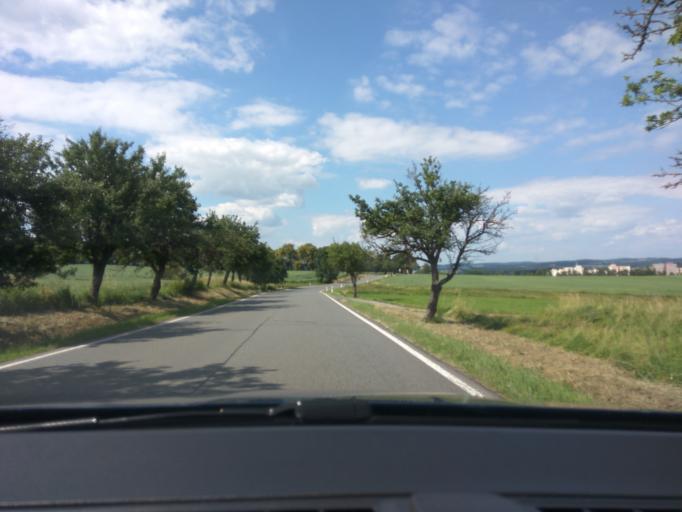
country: CZ
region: Jihocesky
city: Milevsko
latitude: 49.4351
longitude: 14.3584
